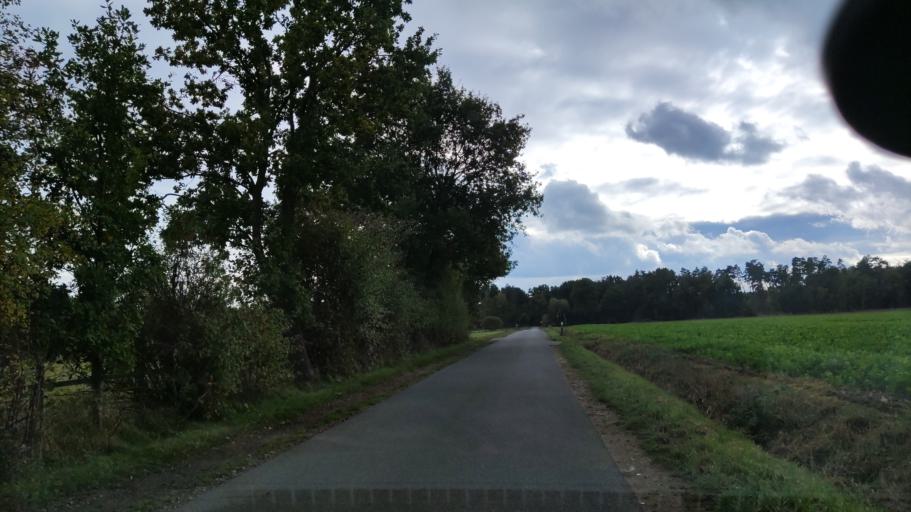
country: DE
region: Lower Saxony
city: Jelmstorf
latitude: 53.1407
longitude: 10.5312
